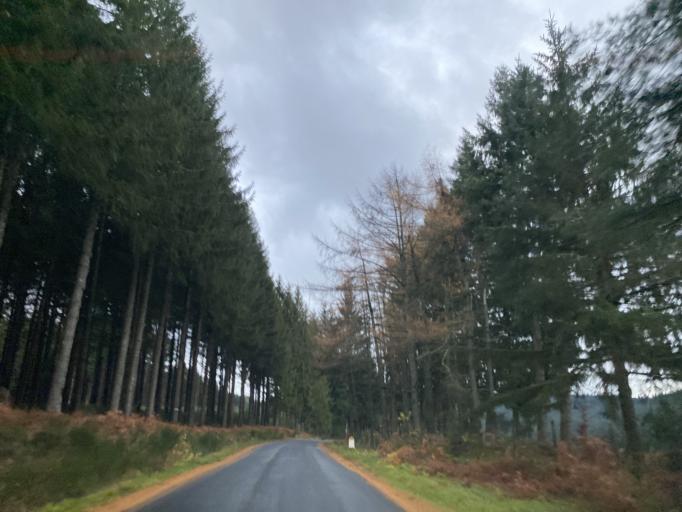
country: FR
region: Auvergne
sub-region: Departement du Puy-de-Dome
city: Cunlhat
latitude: 45.5799
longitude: 3.5597
